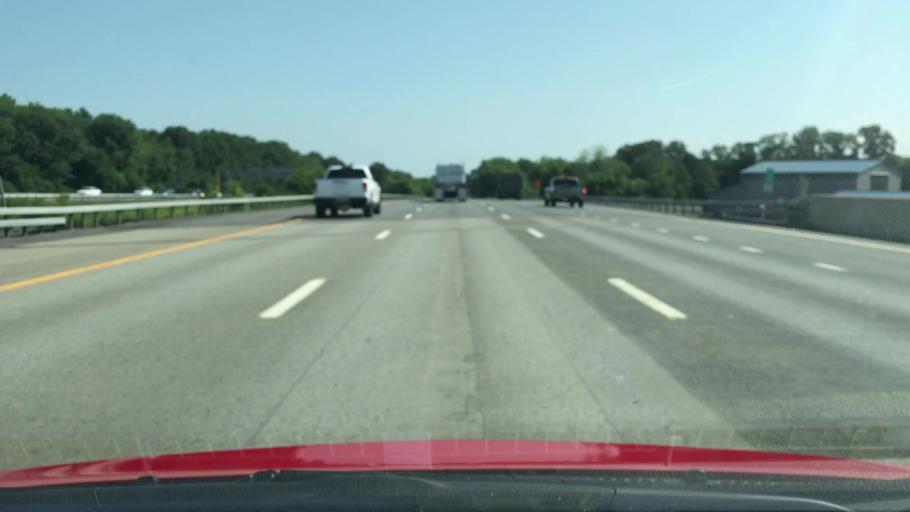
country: US
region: New York
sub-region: Albany County
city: Roessleville
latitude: 42.7385
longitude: -73.7828
